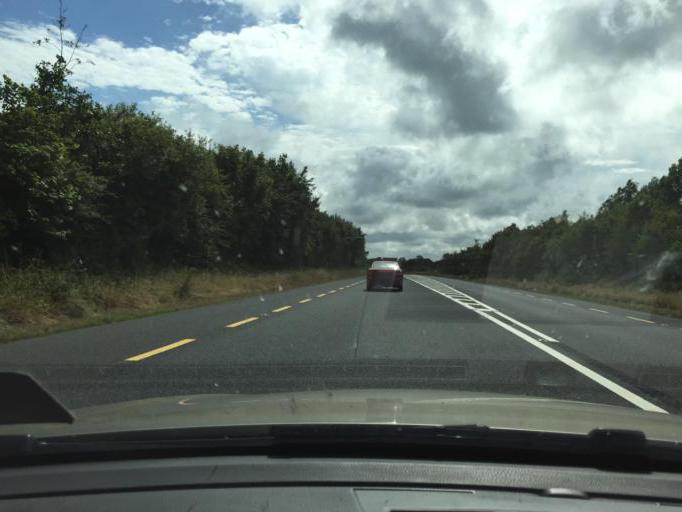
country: IE
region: Munster
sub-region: Waterford
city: Portlaw
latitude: 52.2127
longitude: -7.3915
